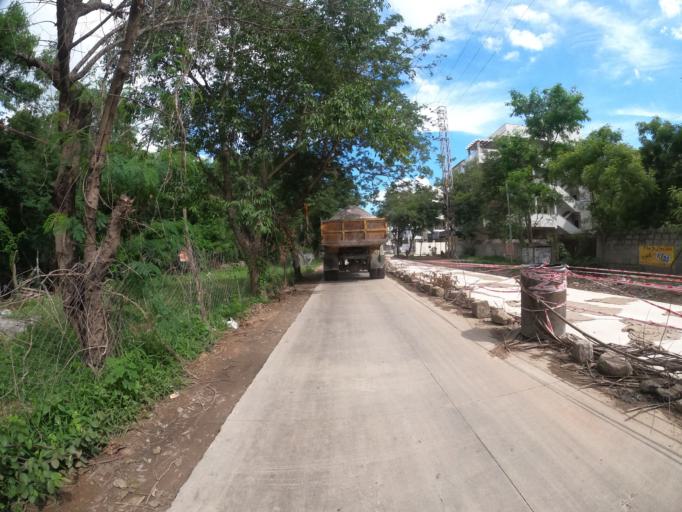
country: IN
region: Telangana
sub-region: Hyderabad
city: Hyderabad
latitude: 17.3551
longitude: 78.3887
